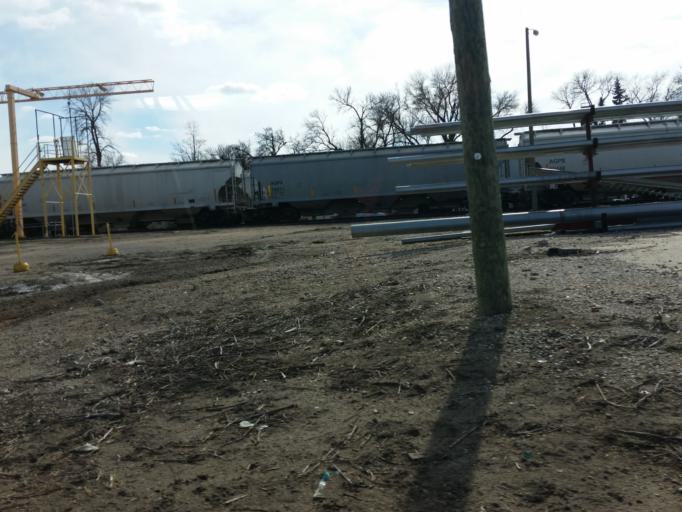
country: US
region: Minnesota
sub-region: Lac qui Parle County
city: Dawson
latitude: 44.9341
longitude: -96.0601
